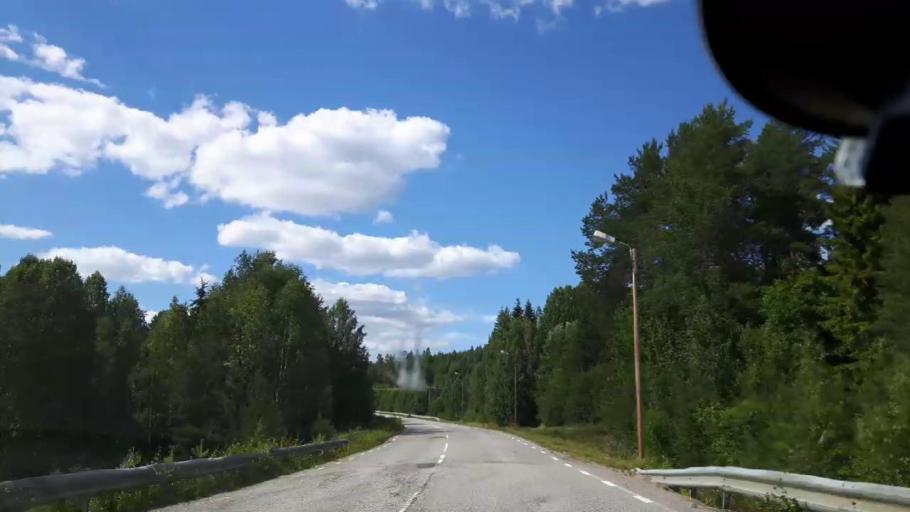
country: SE
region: Vaesternorrland
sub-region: Ange Kommun
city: Fransta
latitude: 62.7895
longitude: 16.2395
